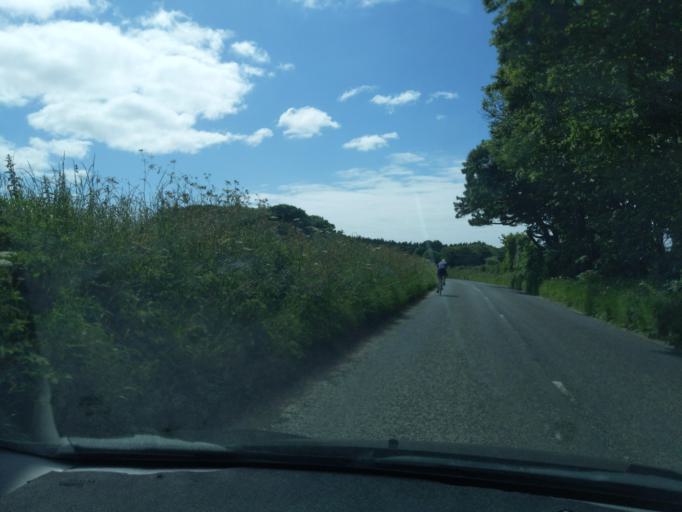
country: GB
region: England
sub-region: Cornwall
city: Perranporth
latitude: 50.2973
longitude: -5.1363
